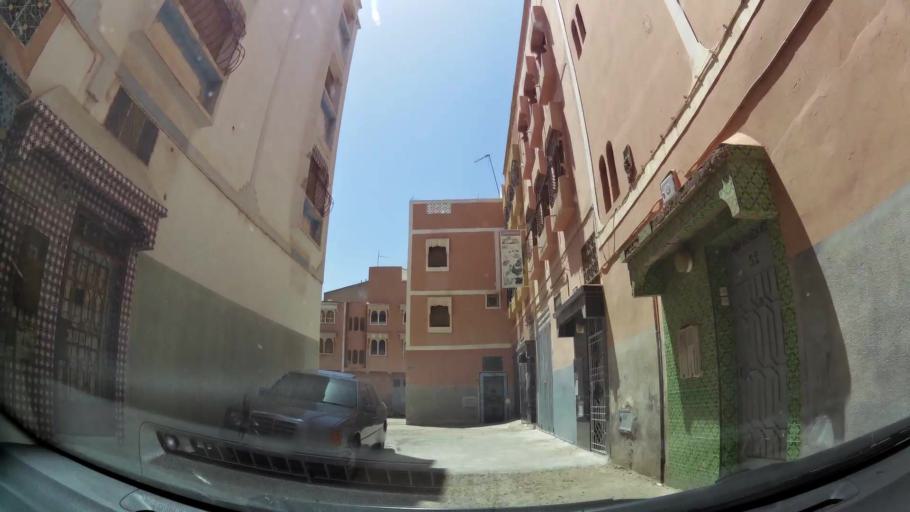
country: MA
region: Souss-Massa-Draa
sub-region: Inezgane-Ait Mellou
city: Inezgane
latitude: 30.3473
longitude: -9.4941
